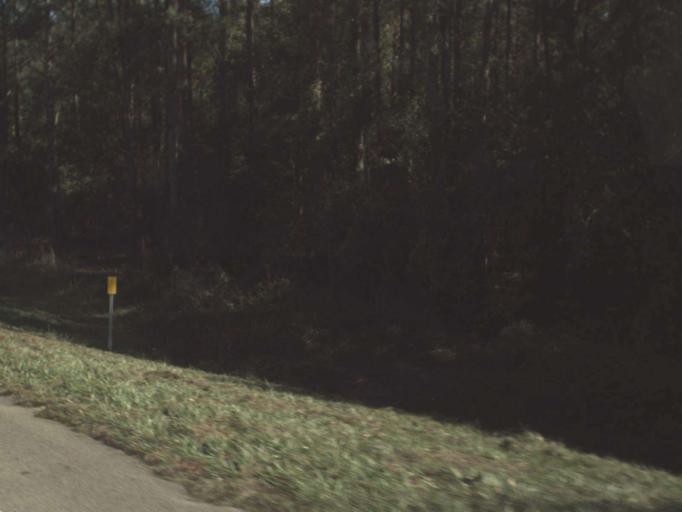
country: US
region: Florida
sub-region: Walton County
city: DeFuniak Springs
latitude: 30.6351
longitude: -85.9380
